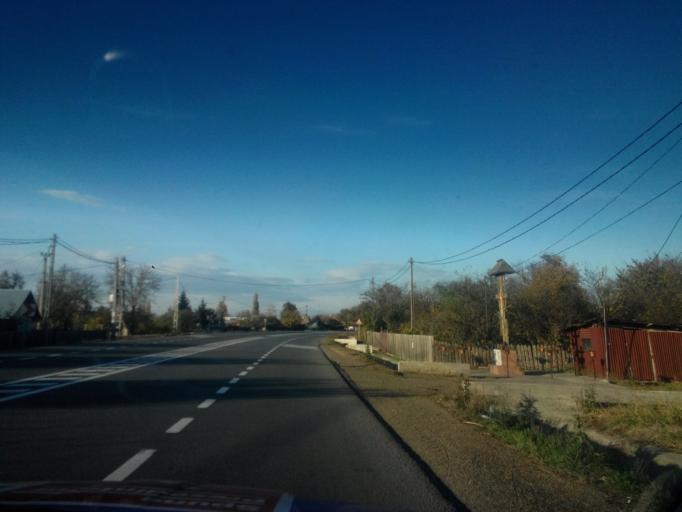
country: RO
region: Neamt
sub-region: Comuna Secueni
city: Secueni
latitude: 46.8467
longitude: 26.8830
